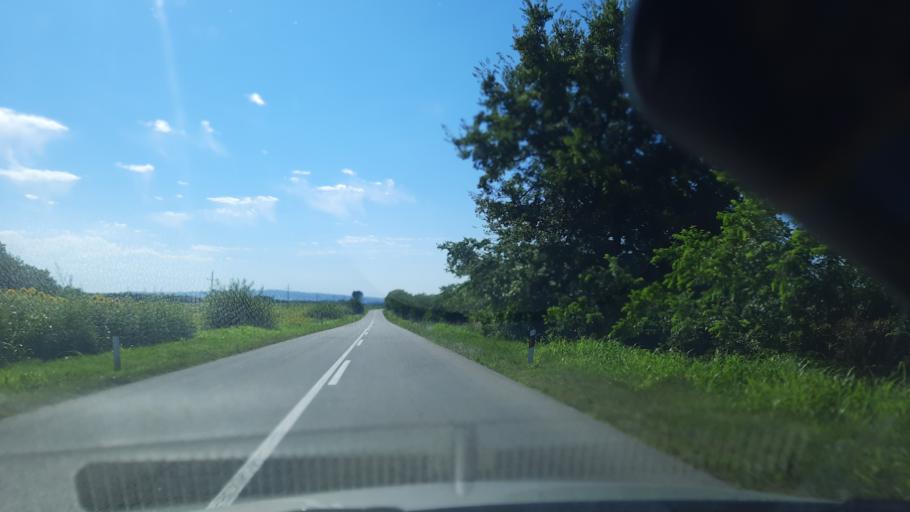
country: RS
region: Central Serbia
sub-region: Branicevski Okrug
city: Pozarevac
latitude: 44.8002
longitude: 21.1883
